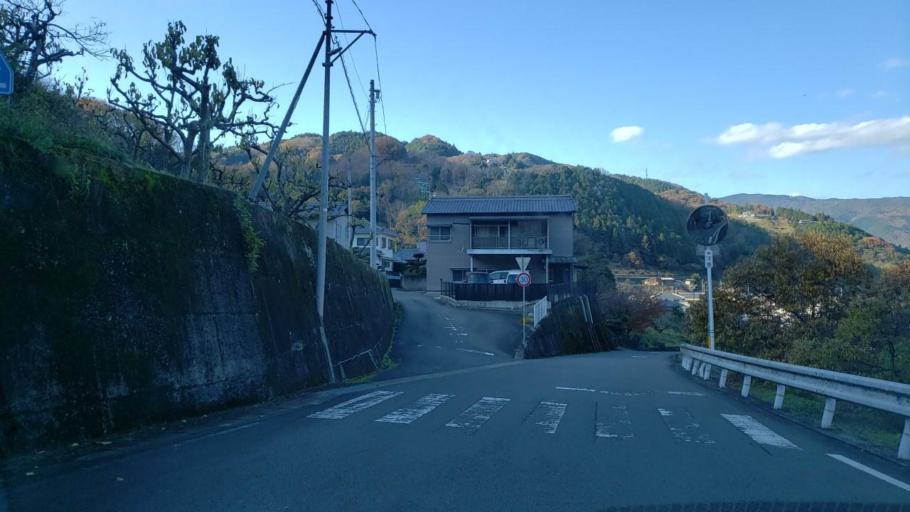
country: JP
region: Tokushima
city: Wakimachi
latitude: 34.0233
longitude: 134.0304
